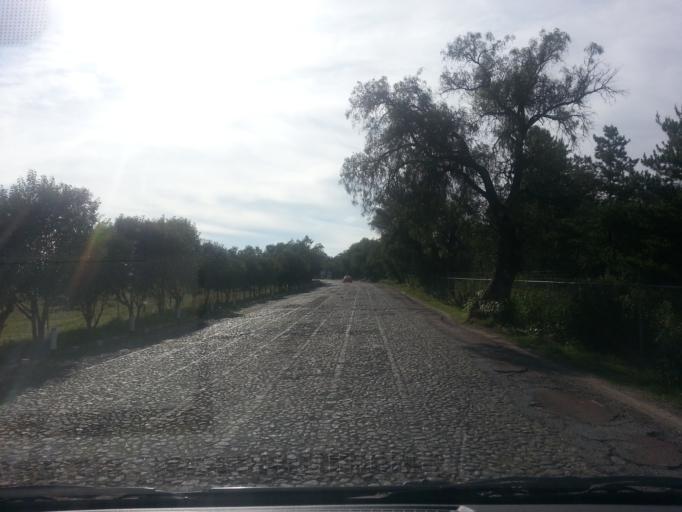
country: MX
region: Morelos
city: Teotihuacan de Arista
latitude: 19.6802
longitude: -98.8526
